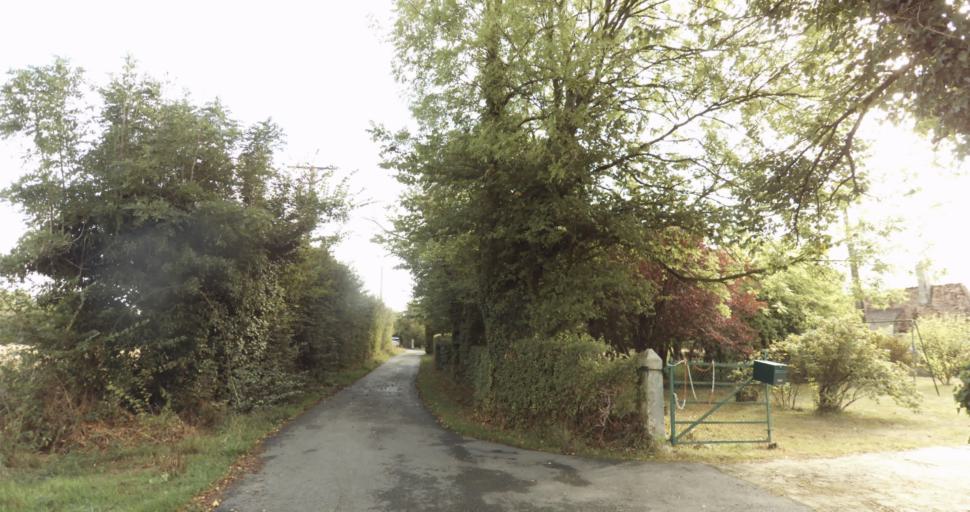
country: FR
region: Lower Normandy
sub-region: Departement de l'Orne
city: Gace
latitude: 48.8502
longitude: 0.2903
